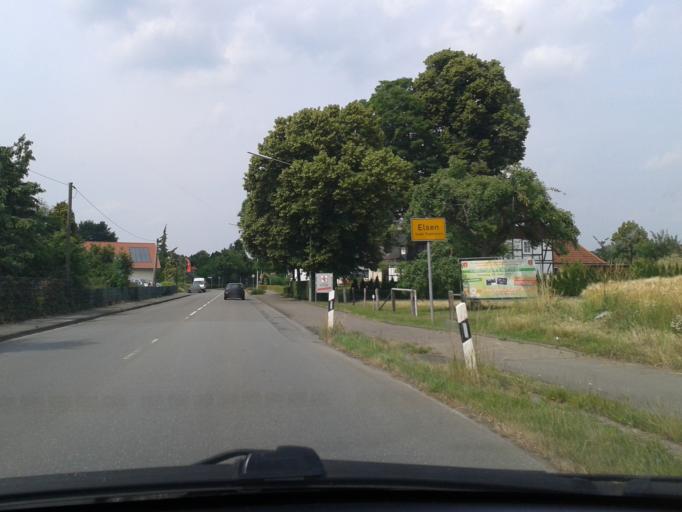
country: DE
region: North Rhine-Westphalia
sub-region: Regierungsbezirk Detmold
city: Paderborn
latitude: 51.7265
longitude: 8.6928
